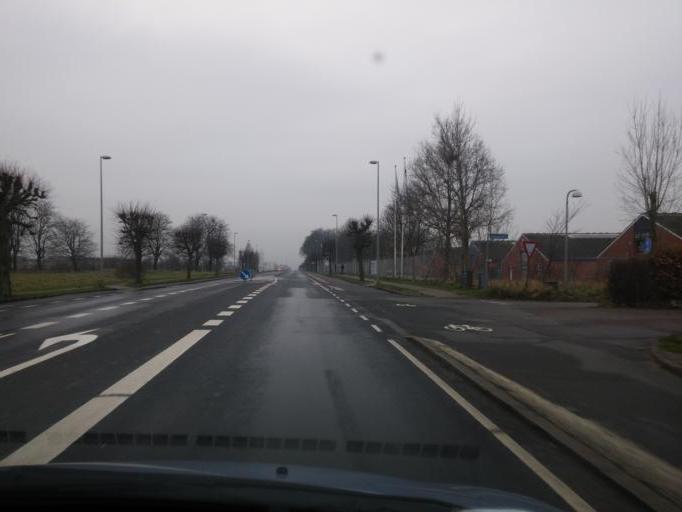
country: DK
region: South Denmark
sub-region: Odense Kommune
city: Neder Holluf
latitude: 55.3914
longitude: 10.4469
